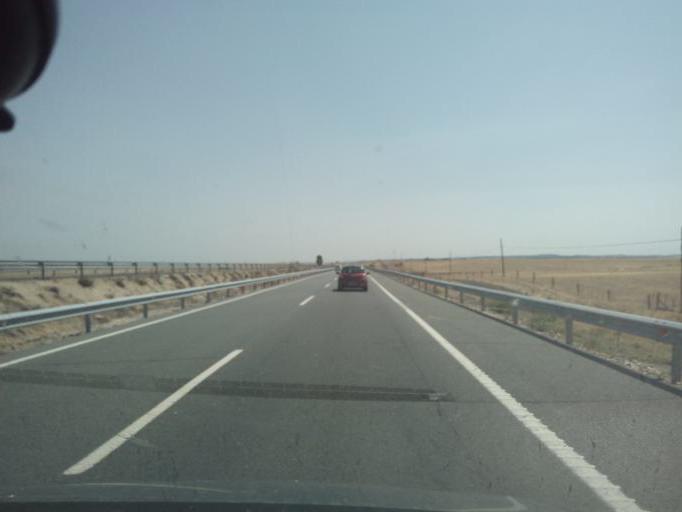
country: ES
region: Extremadura
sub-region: Provincia de Caceres
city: Peraleda de la Mata
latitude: 39.8918
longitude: -5.3971
